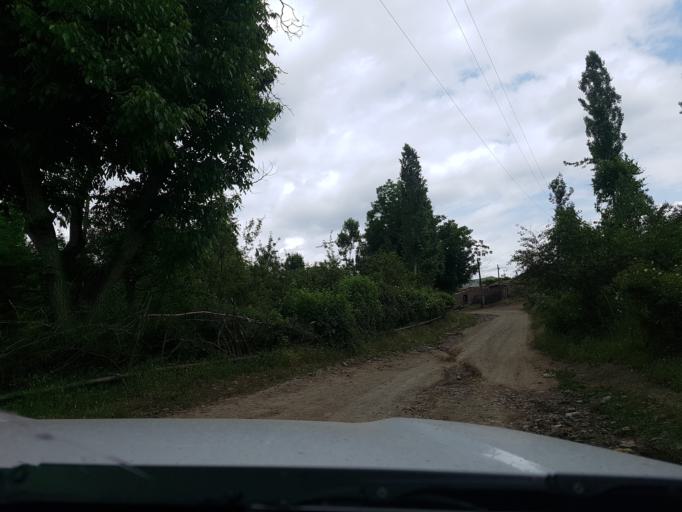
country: TM
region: Ahal
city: Baharly
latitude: 38.1980
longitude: 57.0037
